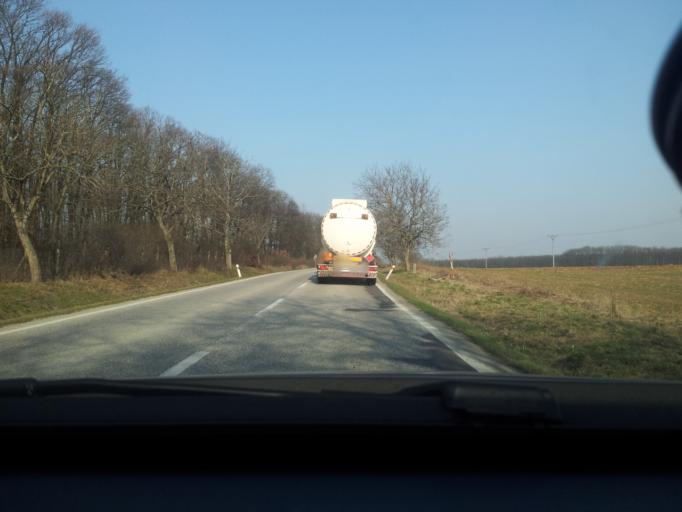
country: SK
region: Nitriansky
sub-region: Okres Nitra
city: Nitra
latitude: 48.3357
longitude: 17.9987
